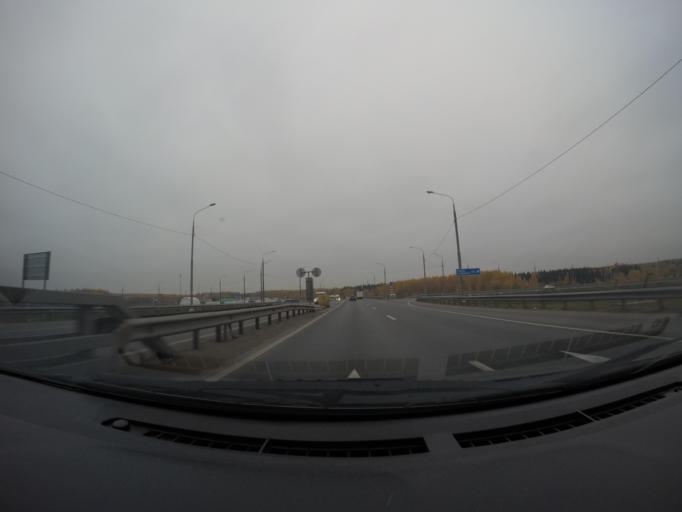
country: RU
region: Moskovskaya
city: Bronnitsy
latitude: 55.4107
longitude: 38.2351
